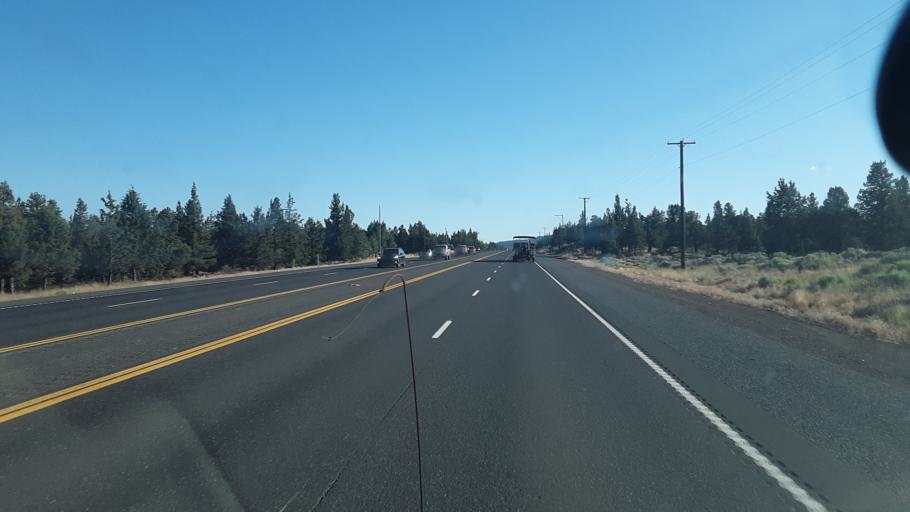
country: US
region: Oregon
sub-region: Deschutes County
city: Bend
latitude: 44.1324
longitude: -121.2796
